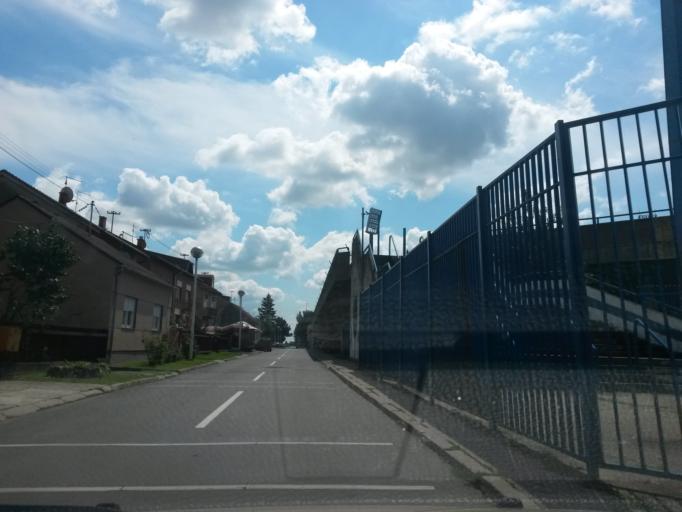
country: HR
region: Osjecko-Baranjska
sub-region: Grad Osijek
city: Osijek
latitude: 45.5460
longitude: 18.6962
